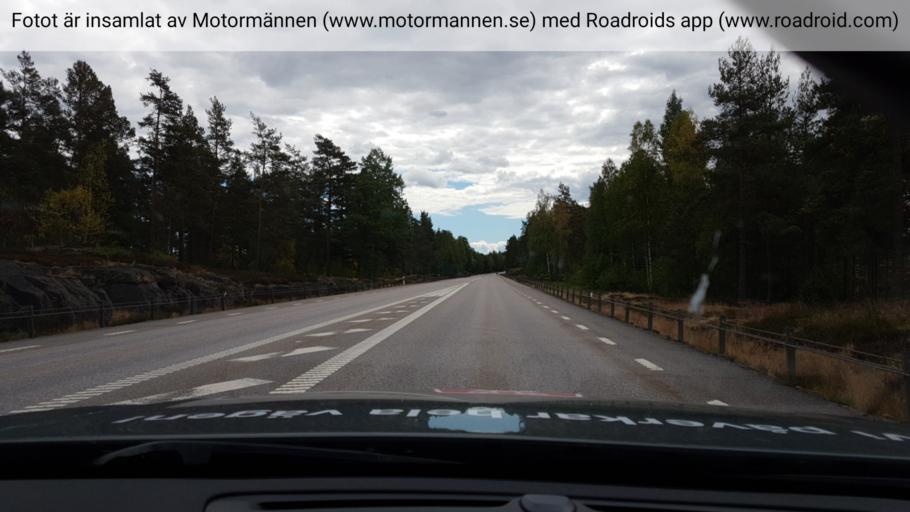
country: SE
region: Kalmar
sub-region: Vasterviks Kommun
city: Ankarsrum
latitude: 57.5231
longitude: 16.4937
